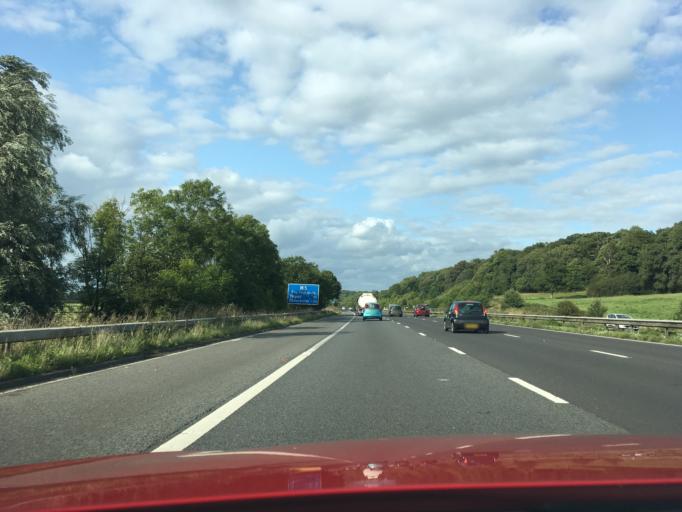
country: GB
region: England
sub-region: South Gloucestershire
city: Falfield
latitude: 51.6430
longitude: -2.4451
